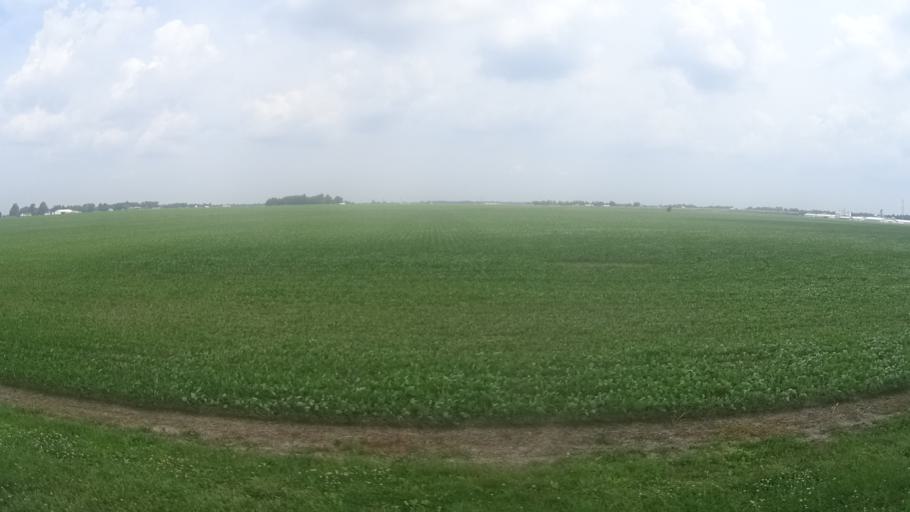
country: US
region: Ohio
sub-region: Huron County
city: Monroeville
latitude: 41.3237
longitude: -82.7119
